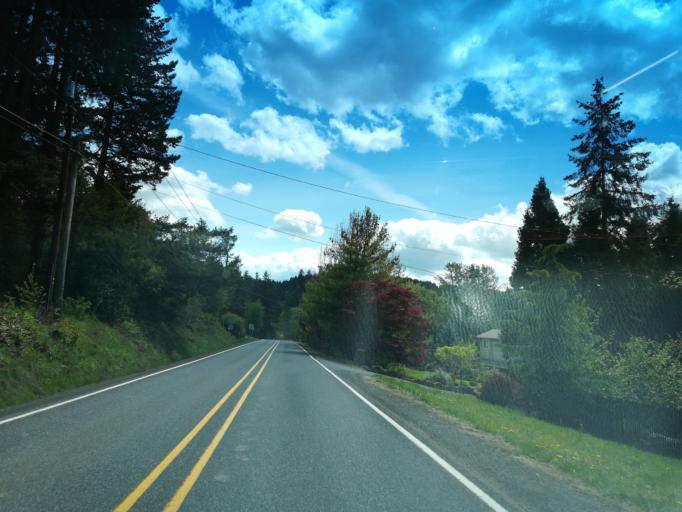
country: US
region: Oregon
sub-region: Clackamas County
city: Damascus
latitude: 45.4403
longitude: -122.4534
